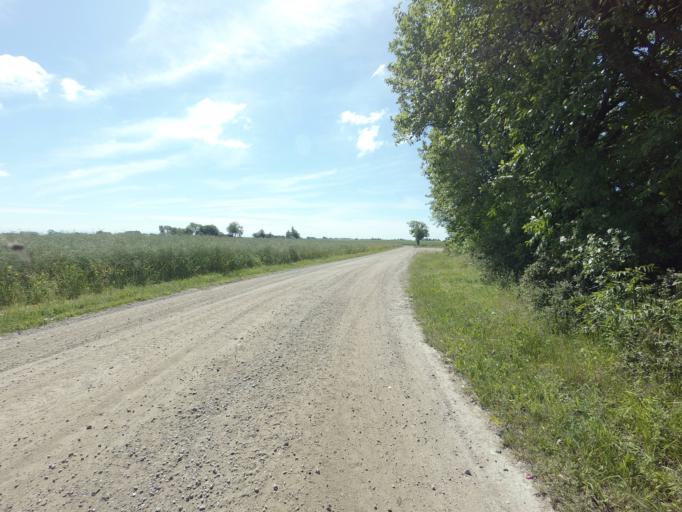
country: SE
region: Skane
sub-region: Trelleborgs Kommun
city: Skare
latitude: 55.4137
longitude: 13.0501
